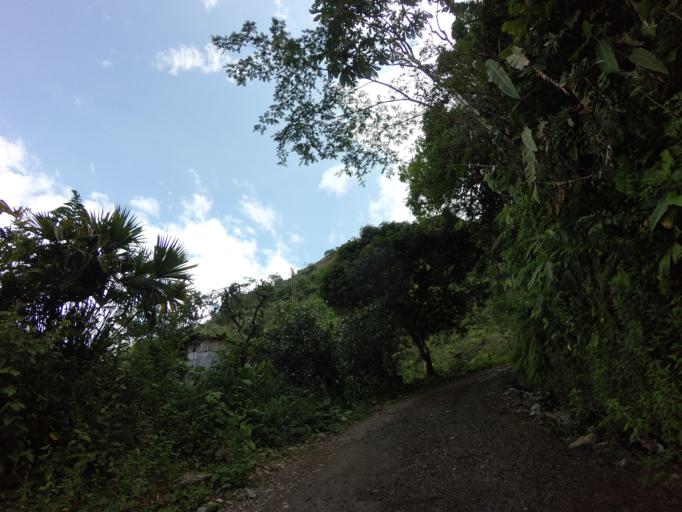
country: CO
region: Antioquia
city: Narino
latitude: 5.5089
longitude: -75.1908
